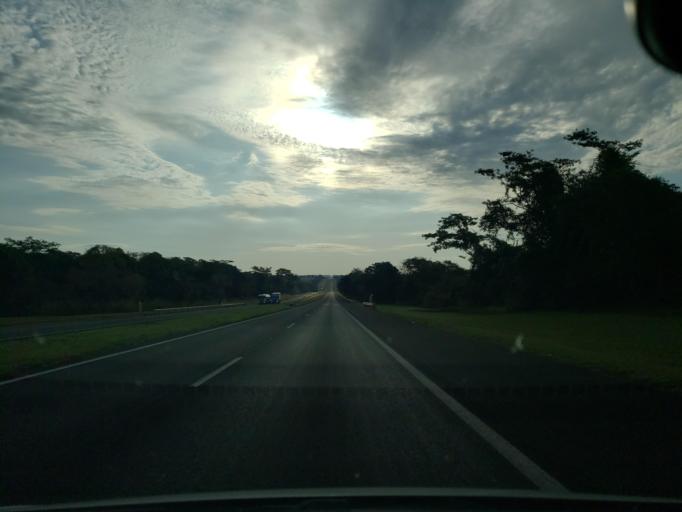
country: BR
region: Sao Paulo
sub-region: Mirandopolis
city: Mirandopolis
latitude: -21.1046
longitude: -51.0336
